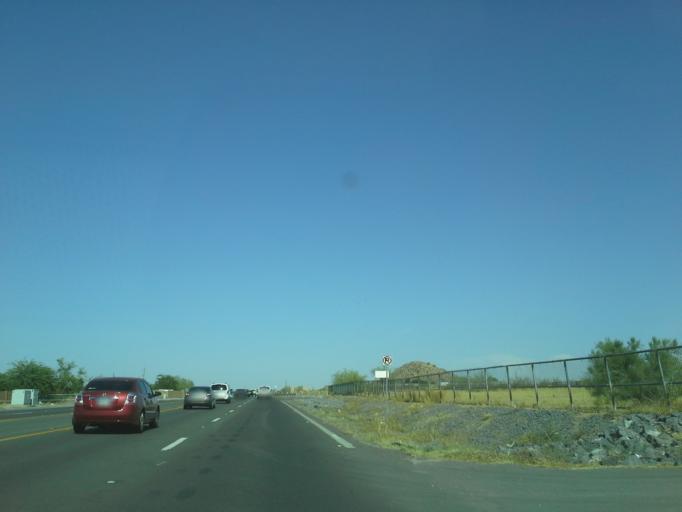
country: US
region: Arizona
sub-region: Maricopa County
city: Queen Creek
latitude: 33.2007
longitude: -111.6269
